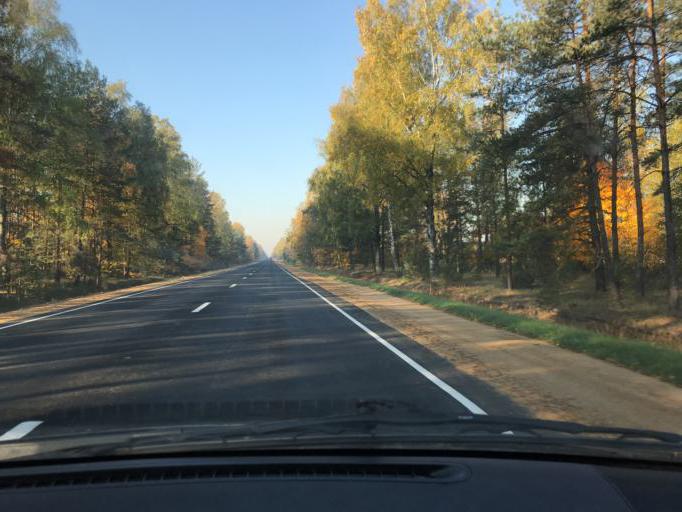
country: BY
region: Brest
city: Baranovichi
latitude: 52.9080
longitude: 25.9127
